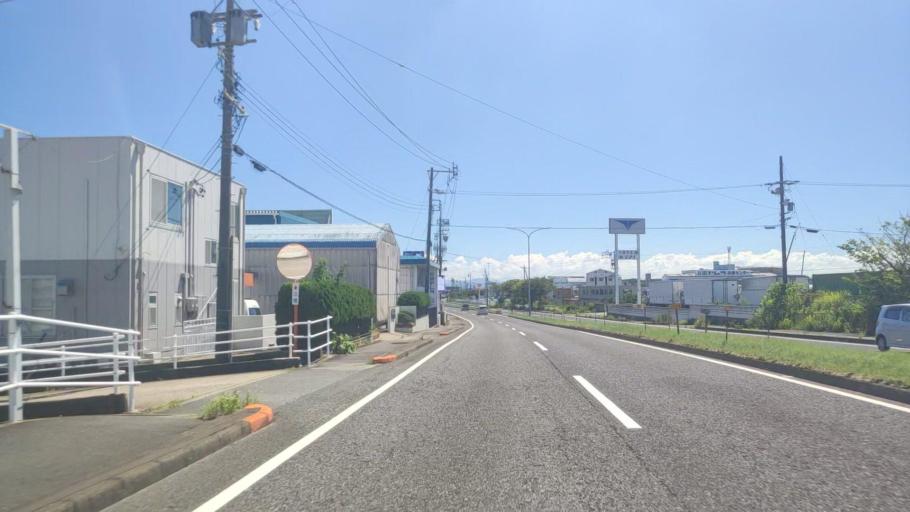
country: JP
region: Mie
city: Kawage
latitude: 34.8075
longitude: 136.5634
